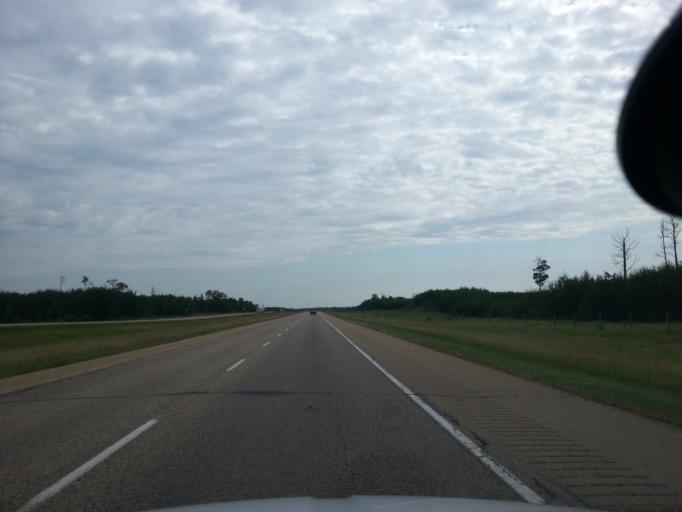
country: CA
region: Alberta
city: Lamont
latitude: 53.5695
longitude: -112.9330
